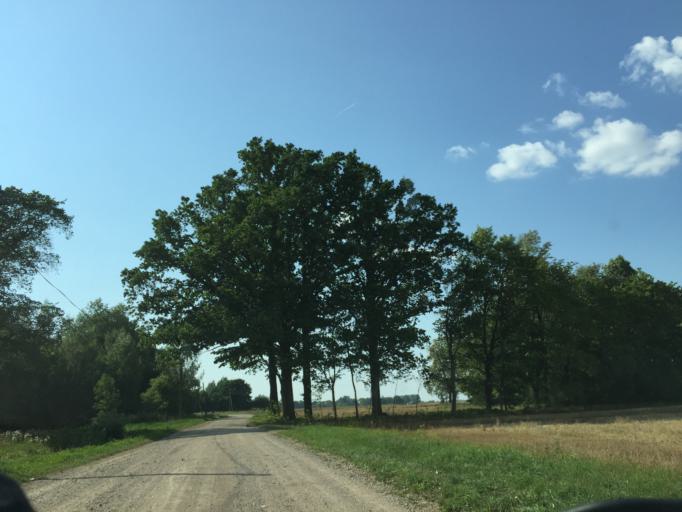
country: LV
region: Jelgava
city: Jelgava
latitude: 56.4527
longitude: 23.7389
